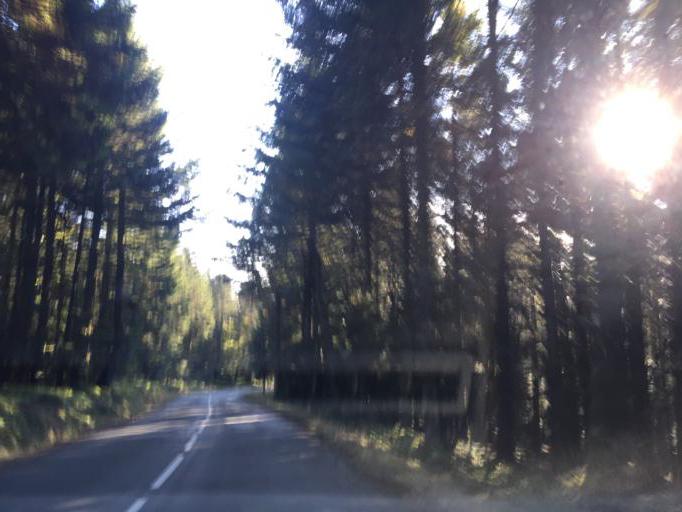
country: FR
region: Rhone-Alpes
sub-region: Departement de la Loire
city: Saint-Julien-Molin-Molette
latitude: 45.3762
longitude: 4.5636
